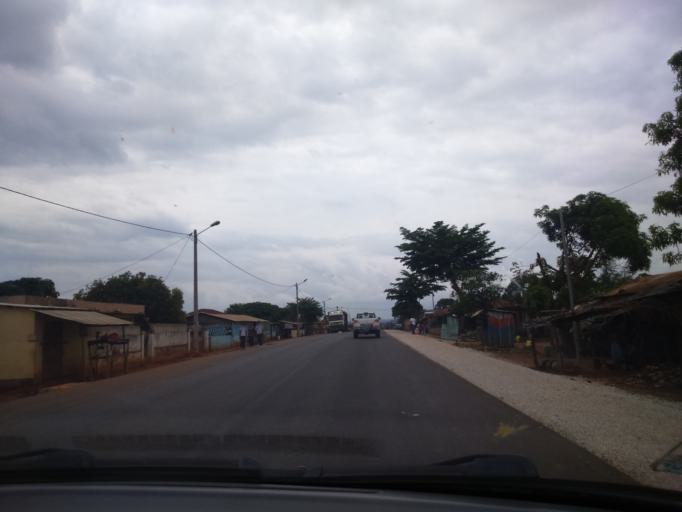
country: CI
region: Lagunes
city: Akoupe
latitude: 6.3410
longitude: -3.8534
